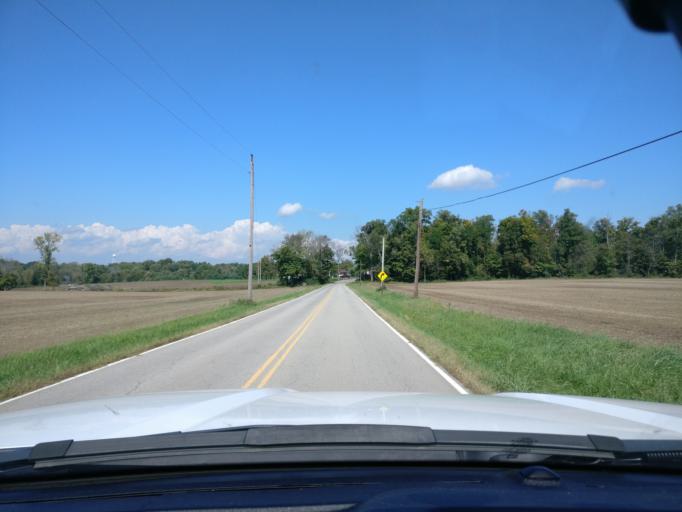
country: US
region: Ohio
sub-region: Warren County
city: Waynesville
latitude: 39.4938
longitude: -84.0023
